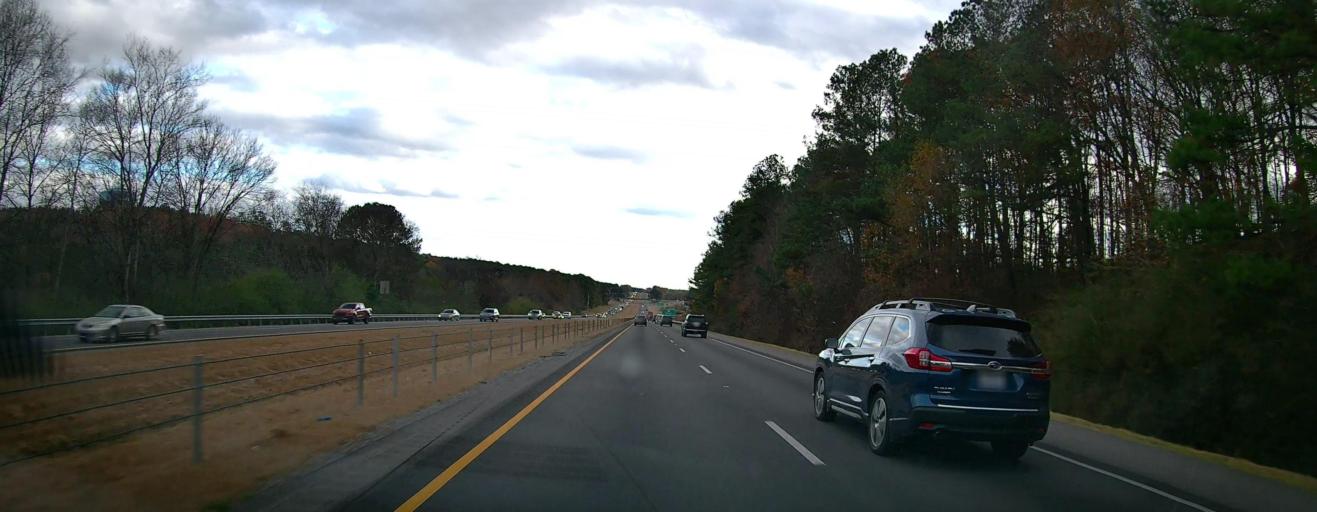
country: US
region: Alabama
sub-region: Cullman County
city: Cullman
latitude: 34.1819
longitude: -86.8776
